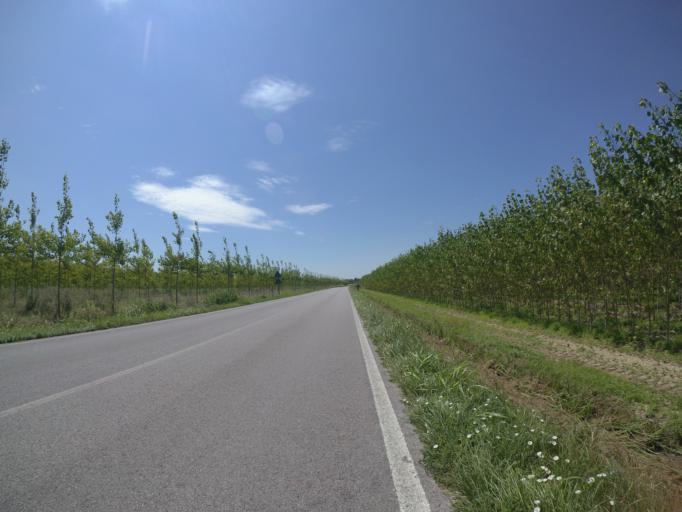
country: IT
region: Friuli Venezia Giulia
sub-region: Provincia di Udine
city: Talmassons
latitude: 45.8897
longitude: 13.1261
